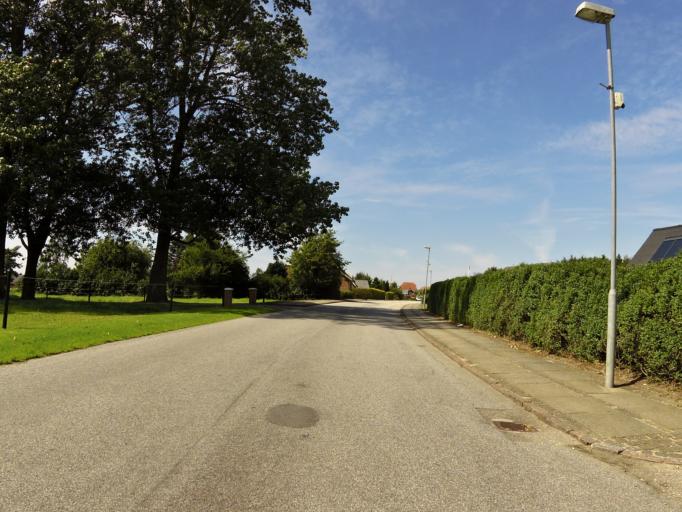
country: DK
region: South Denmark
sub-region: Haderslev Kommune
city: Gram
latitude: 55.2456
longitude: 8.9739
